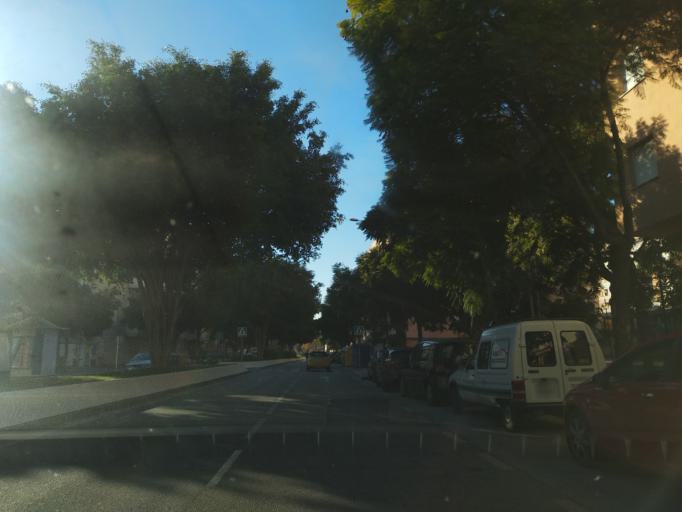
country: ES
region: Andalusia
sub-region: Provincia de Malaga
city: Malaga
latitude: 36.7452
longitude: -4.4266
